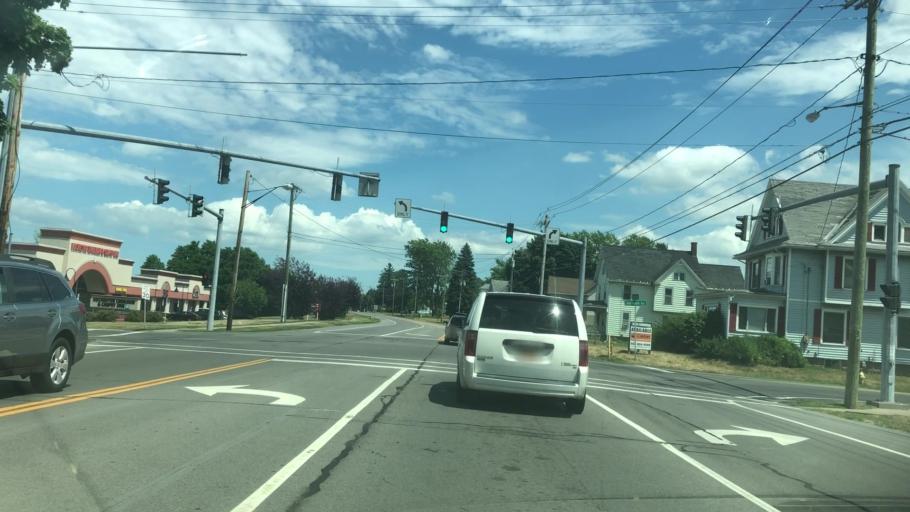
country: US
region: New York
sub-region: Monroe County
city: Webster
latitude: 43.2105
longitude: -77.4435
